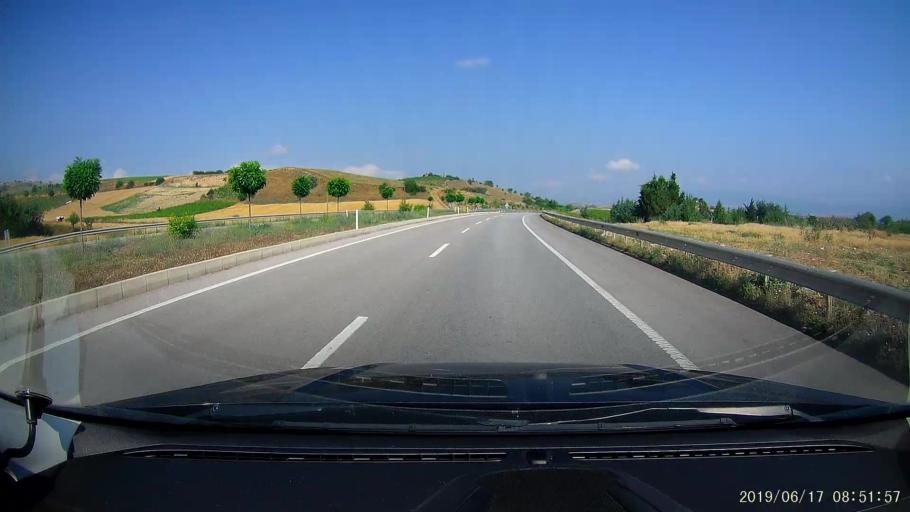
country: TR
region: Tokat
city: Erbaa
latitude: 40.6918
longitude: 36.5053
